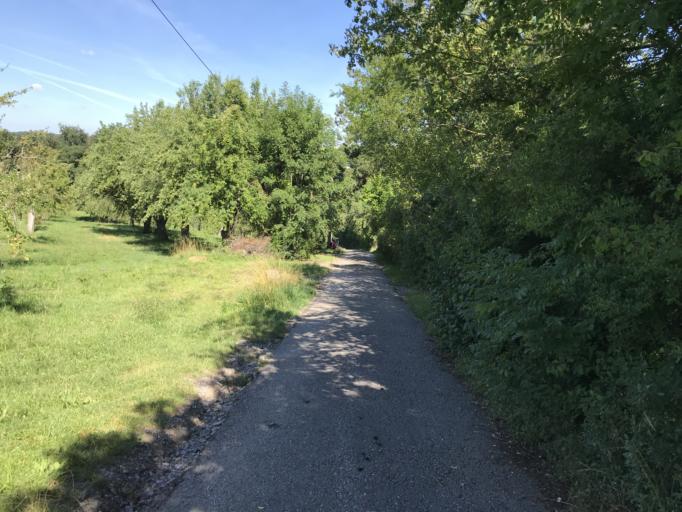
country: DE
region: Baden-Wuerttemberg
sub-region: Regierungsbezirk Stuttgart
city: Stuttgart
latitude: 48.7464
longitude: 9.1512
